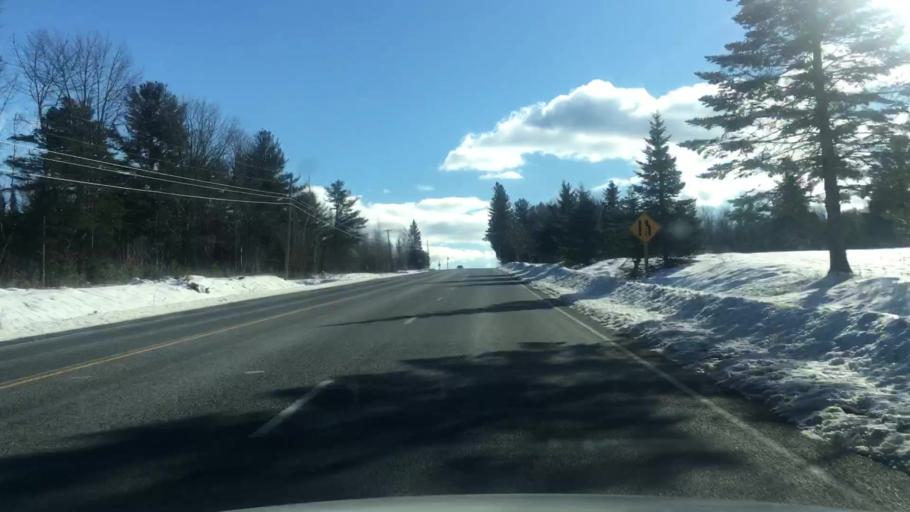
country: US
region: Maine
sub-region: Somerset County
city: Madison
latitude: 44.8957
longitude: -69.8093
